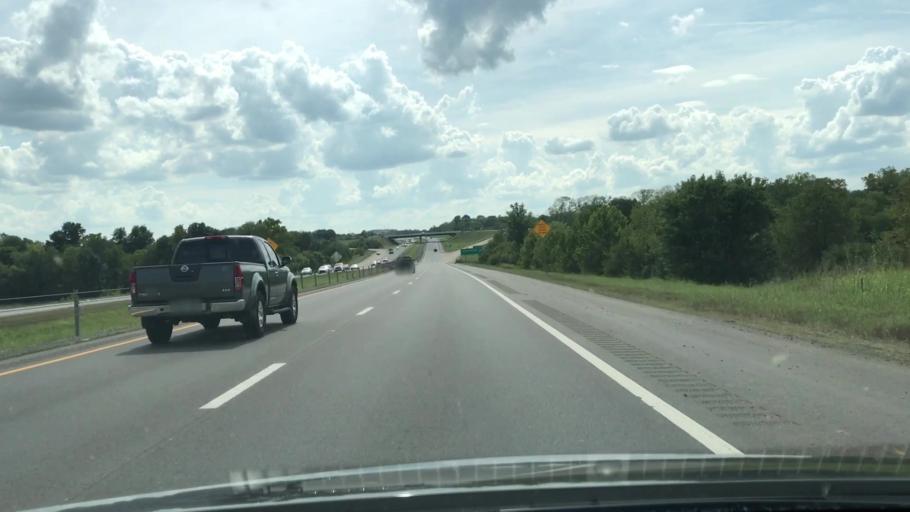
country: US
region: Tennessee
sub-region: Sumner County
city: Gallatin
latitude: 36.3835
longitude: -86.4958
